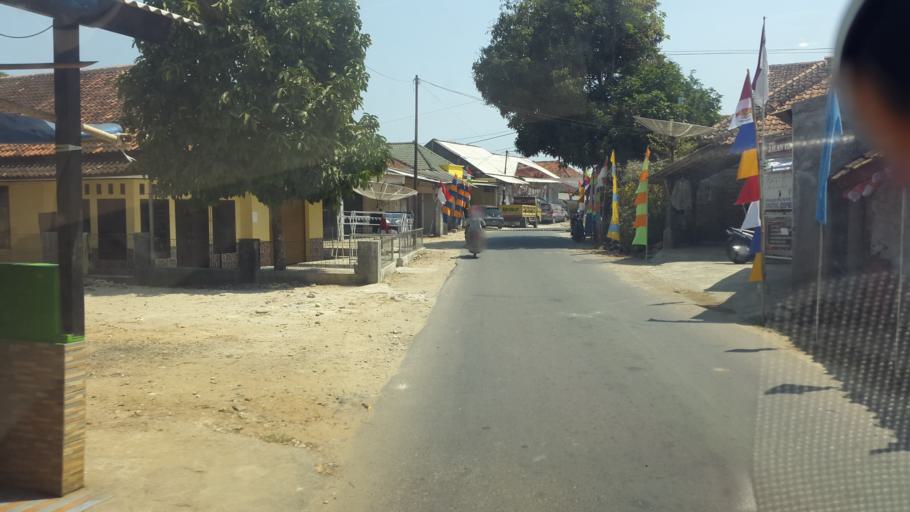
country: ID
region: West Java
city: Ciracap
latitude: -7.3313
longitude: 106.5204
